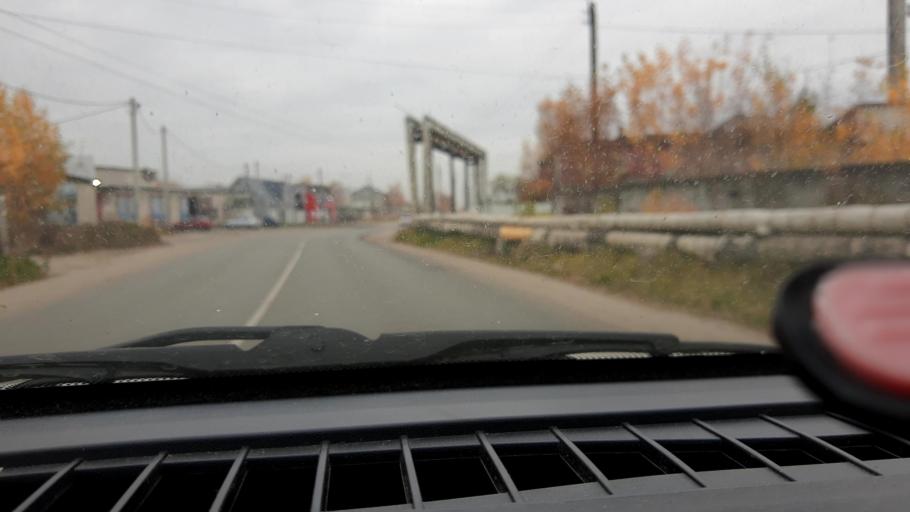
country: RU
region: Nizjnij Novgorod
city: Gorodets
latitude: 56.6440
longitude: 43.4890
